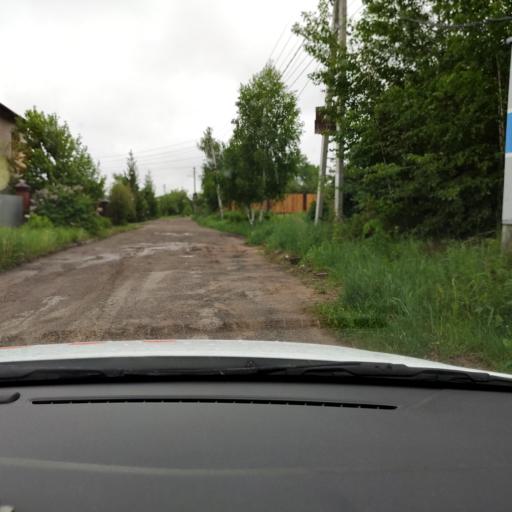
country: RU
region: Tatarstan
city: Stolbishchi
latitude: 55.7535
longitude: 49.2560
